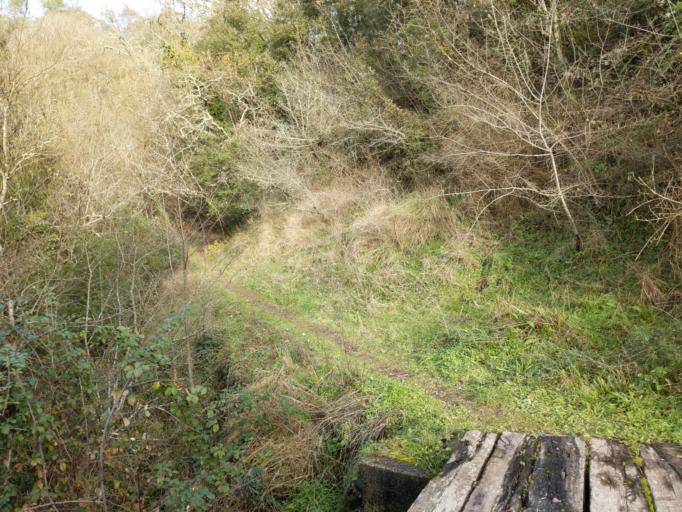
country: FR
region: Provence-Alpes-Cote d'Azur
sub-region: Departement du Var
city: Bagnols-en-Foret
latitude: 43.5394
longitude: 6.6950
